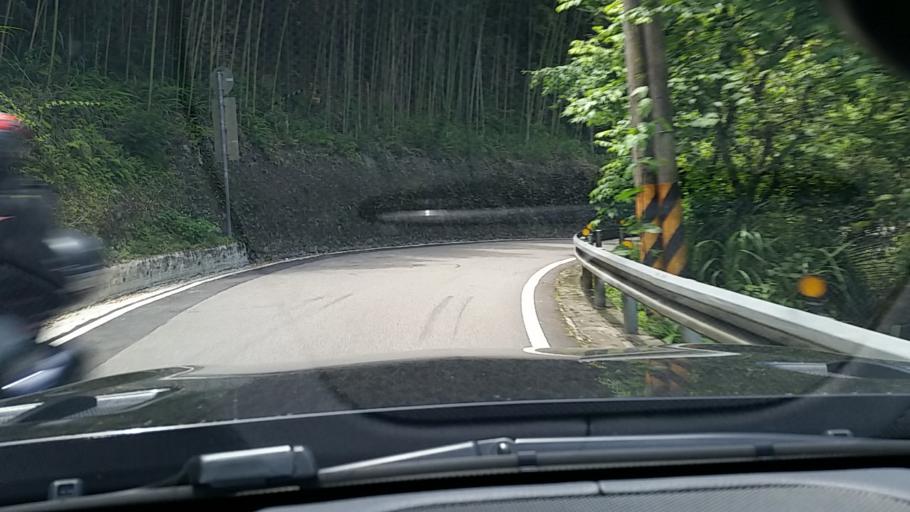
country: TW
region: Taiwan
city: Daxi
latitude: 24.6990
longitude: 121.3653
